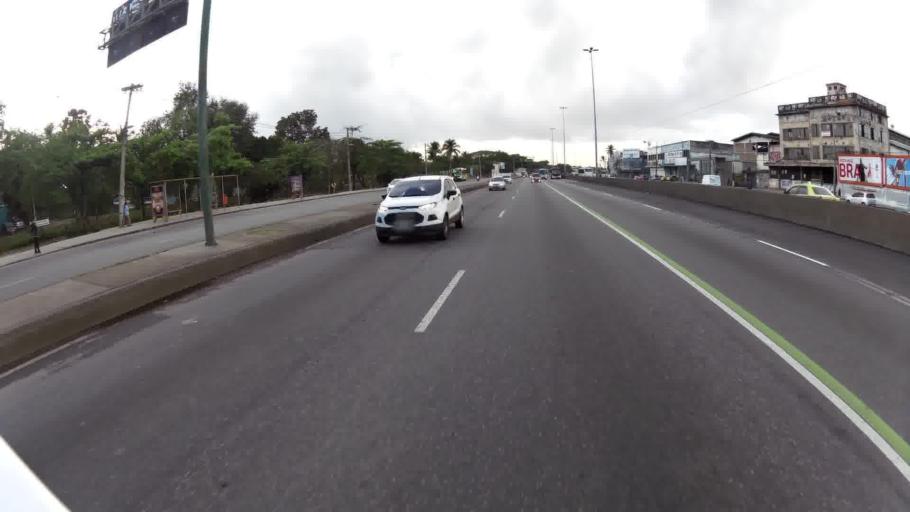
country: BR
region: Rio de Janeiro
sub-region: Duque De Caxias
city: Duque de Caxias
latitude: -22.8370
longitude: -43.2578
